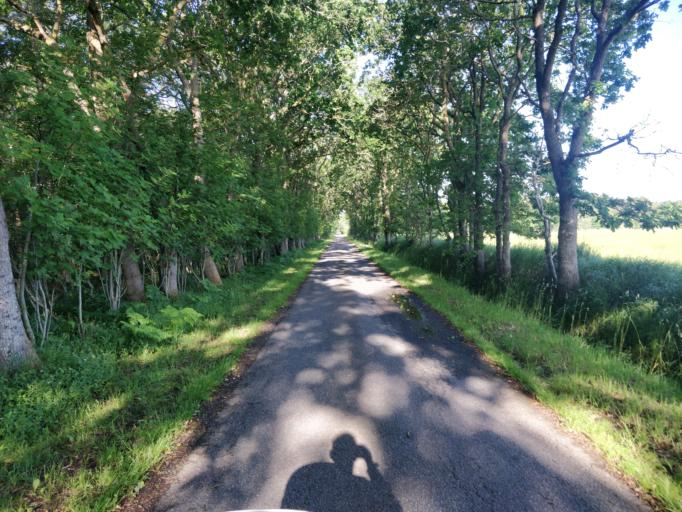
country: DK
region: North Denmark
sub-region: Laeso Kommune
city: Byrum
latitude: 57.2769
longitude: 10.9240
